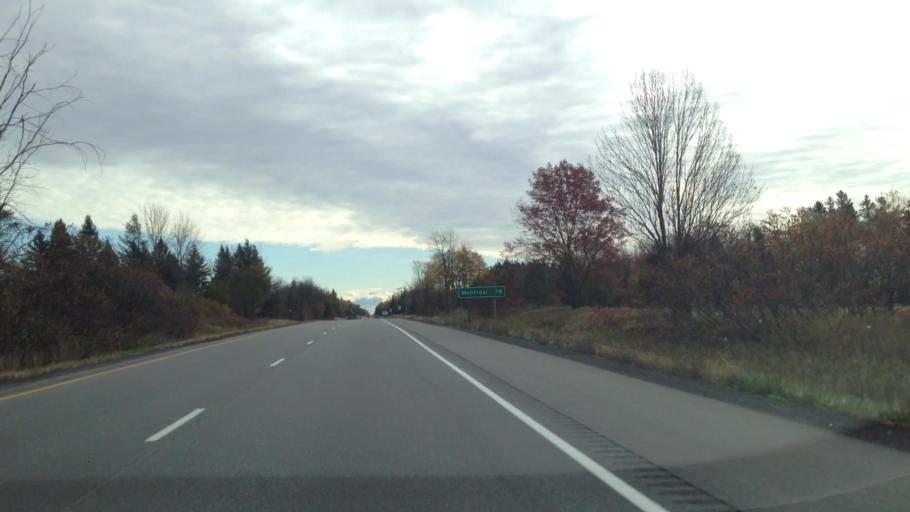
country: CA
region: Ontario
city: Hawkesbury
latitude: 45.5625
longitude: -74.4880
